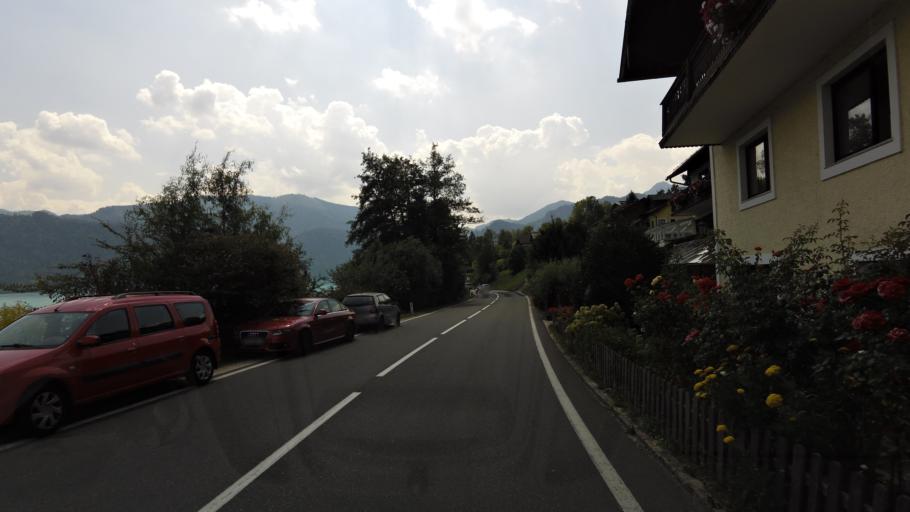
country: AT
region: Upper Austria
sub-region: Politischer Bezirk Vocklabruck
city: Steinbach am Attersee
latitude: 47.8195
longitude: 13.5086
